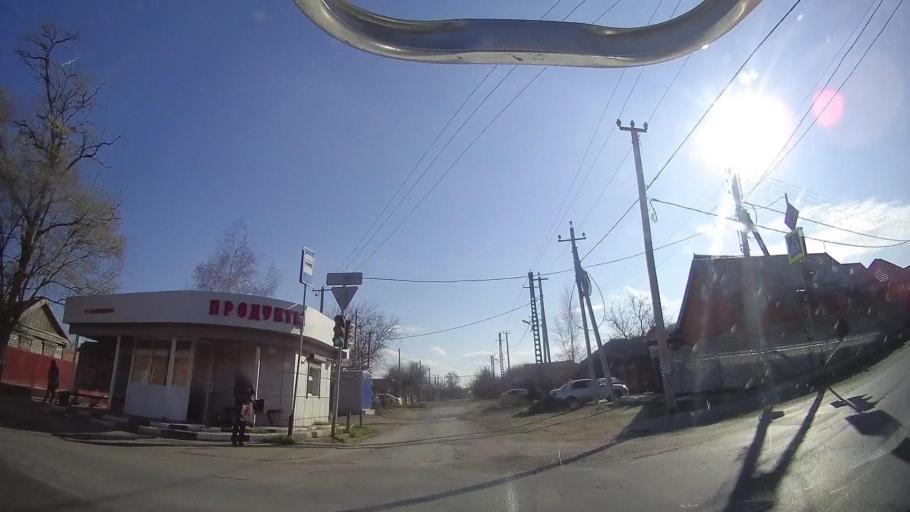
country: RU
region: Rostov
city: Bataysk
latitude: 47.1167
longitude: 39.6841
